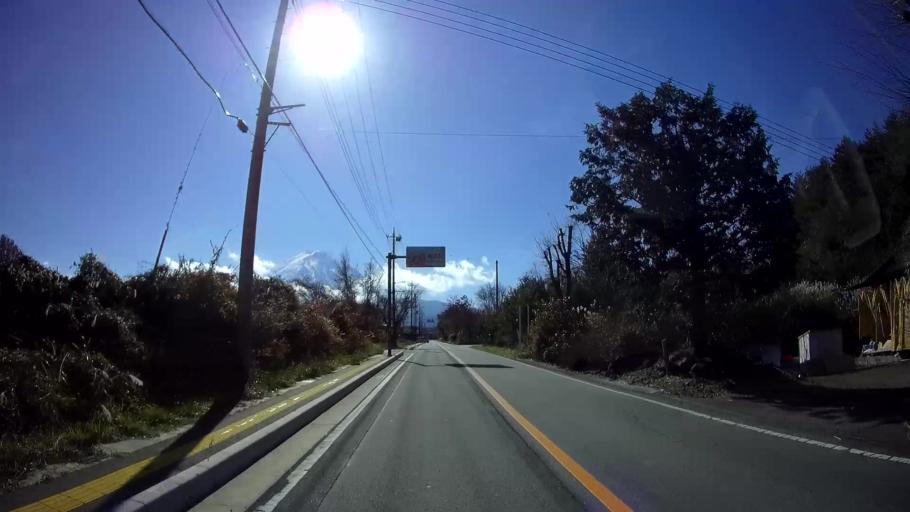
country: JP
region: Yamanashi
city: Fujikawaguchiko
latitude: 35.4906
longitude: 138.7280
